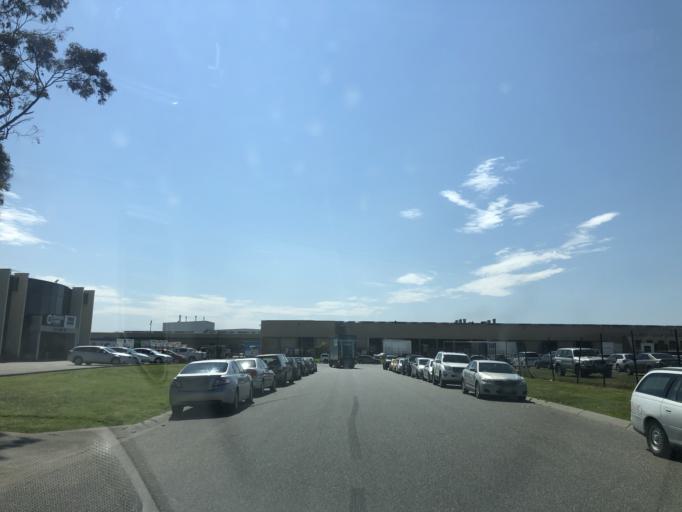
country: AU
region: Victoria
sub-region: Casey
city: Hampton Park
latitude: -38.0310
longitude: 145.2402
